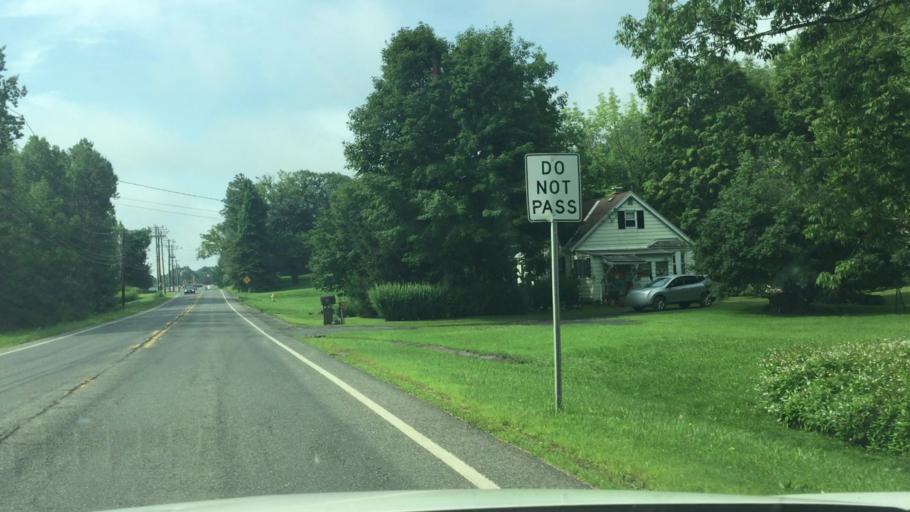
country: US
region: Massachusetts
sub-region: Berkshire County
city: Richmond
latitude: 42.4221
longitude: -73.3346
